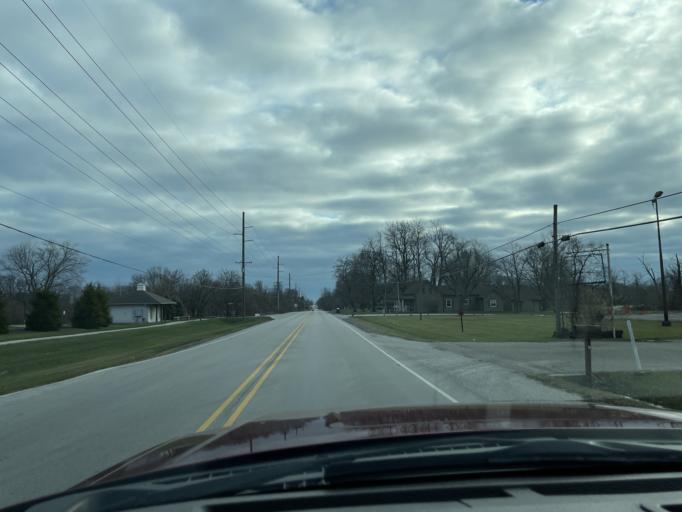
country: US
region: Indiana
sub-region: Hendricks County
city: Avon
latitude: 39.7620
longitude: -86.4566
